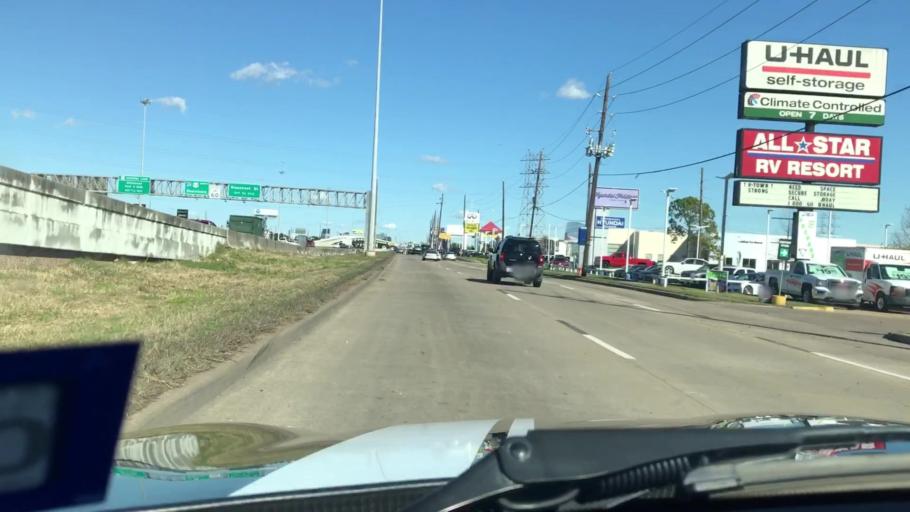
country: US
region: Texas
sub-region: Fort Bend County
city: Meadows Place
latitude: 29.6647
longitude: -95.5533
